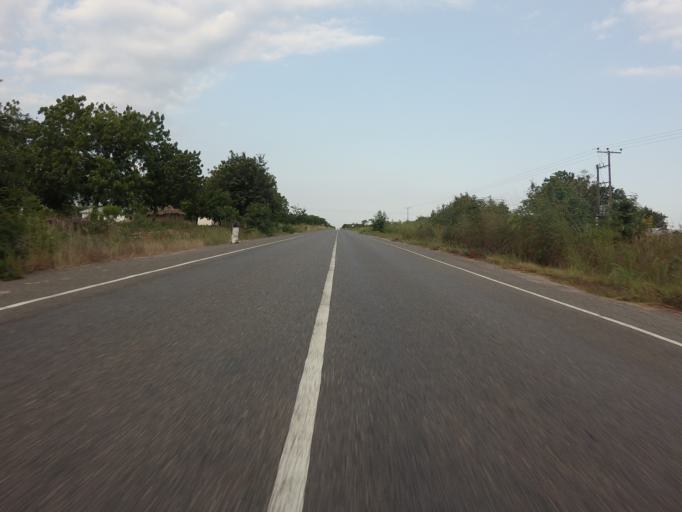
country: GH
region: Volta
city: Anloga
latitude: 6.0874
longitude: 0.5438
